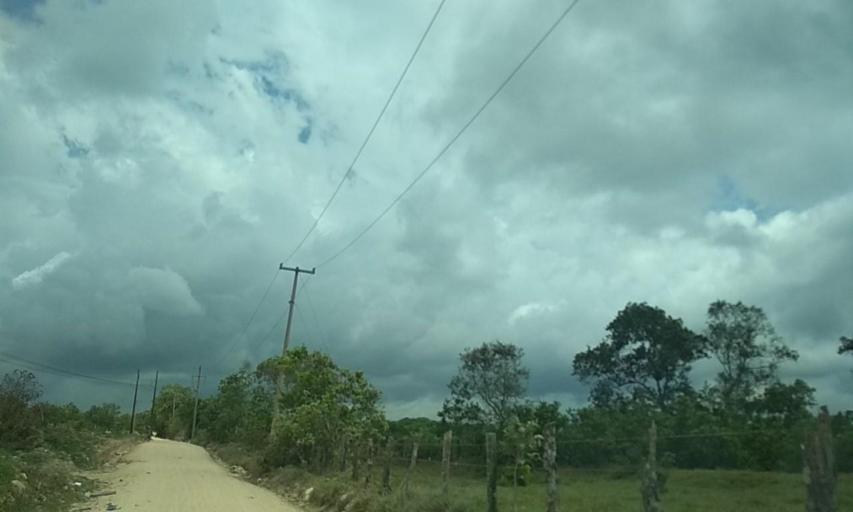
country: MX
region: Veracruz
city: Las Choapas
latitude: 17.9008
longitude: -94.1225
